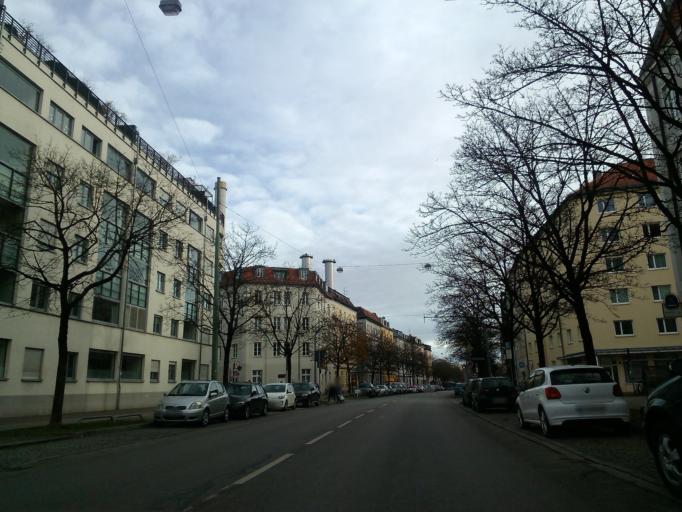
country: DE
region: Bavaria
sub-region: Upper Bavaria
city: Munich
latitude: 48.1122
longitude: 11.5501
